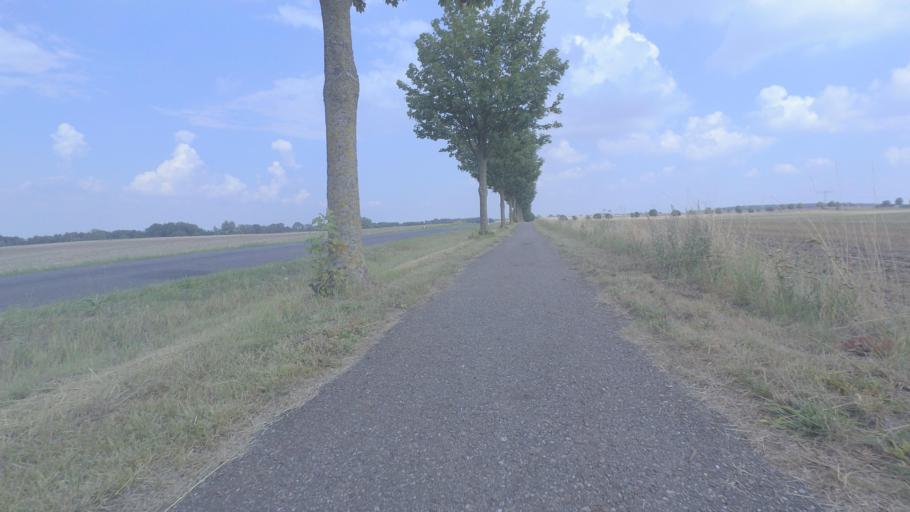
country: DE
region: Mecklenburg-Vorpommern
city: Neukalen
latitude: 53.7703
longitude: 12.8529
